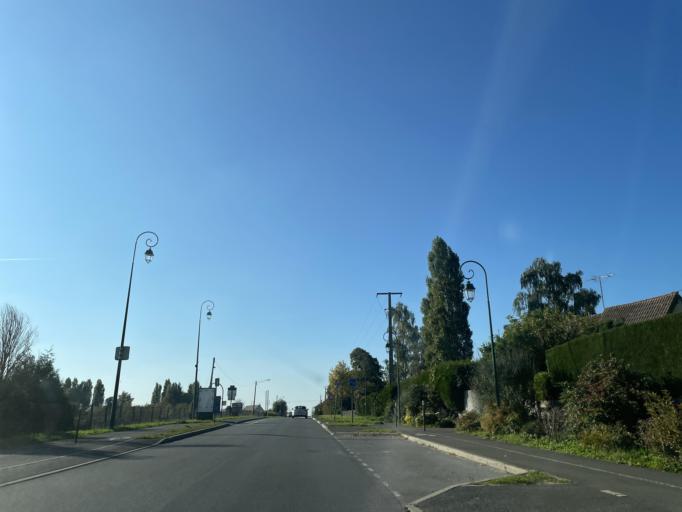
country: FR
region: Ile-de-France
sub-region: Departement de Seine-et-Marne
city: Pommeuse
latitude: 48.8295
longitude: 3.0238
